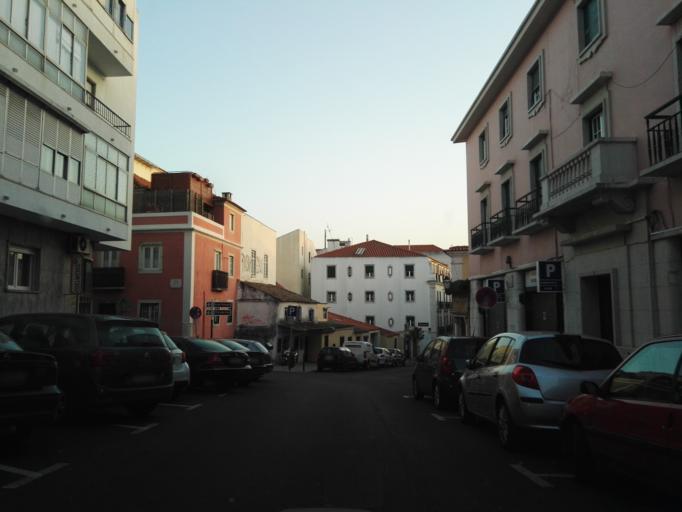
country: PT
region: Lisbon
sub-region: Lisbon
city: Lisbon
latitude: 38.7133
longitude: -9.1512
